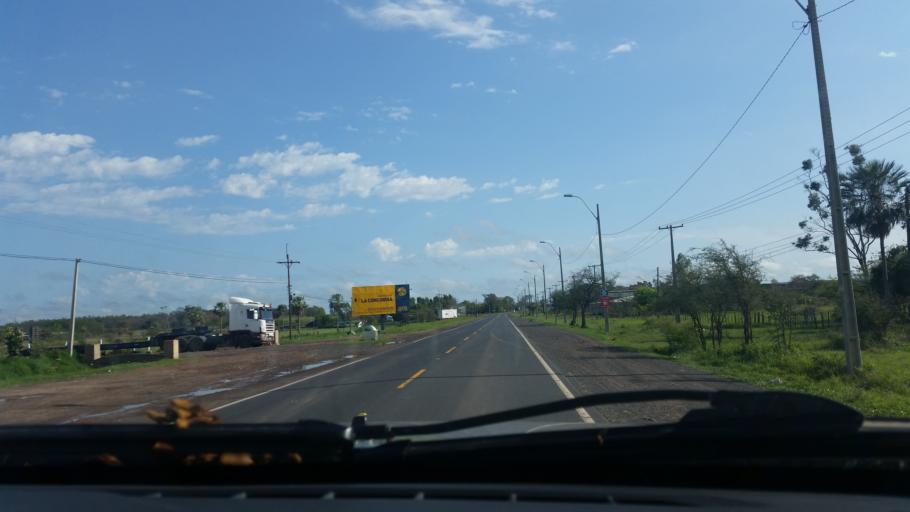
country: PY
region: Presidente Hayes
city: Villa Hayes
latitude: -25.0681
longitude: -57.5331
